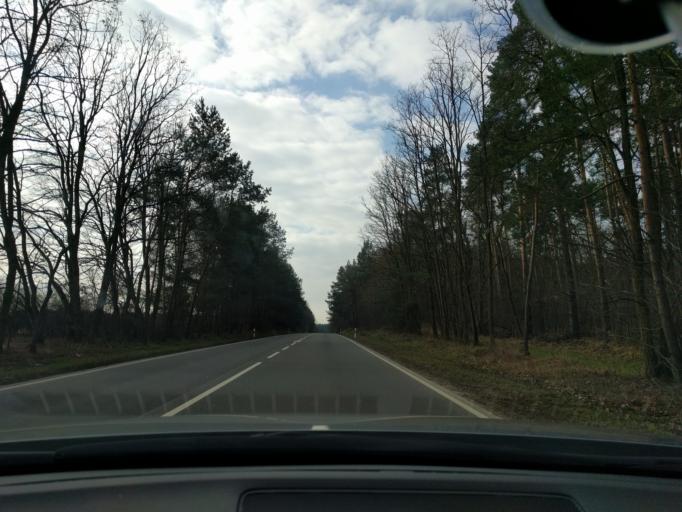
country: DE
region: Saxony-Anhalt
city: Colbitz
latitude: 52.3814
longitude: 11.6191
